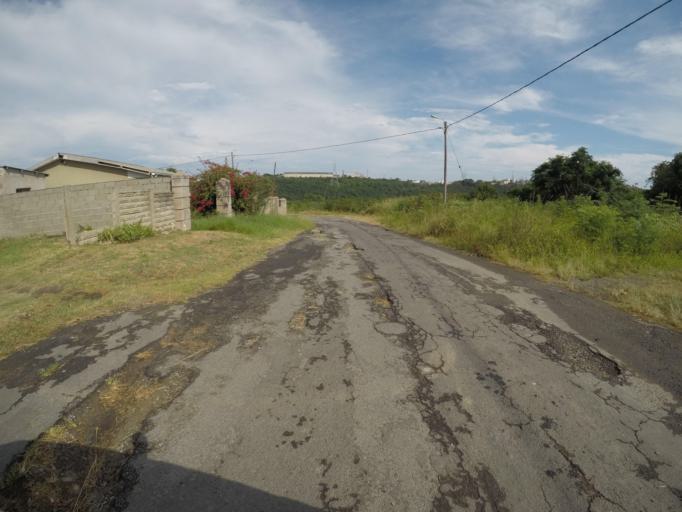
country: ZA
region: Eastern Cape
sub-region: Buffalo City Metropolitan Municipality
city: East London
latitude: -33.0237
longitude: 27.8810
